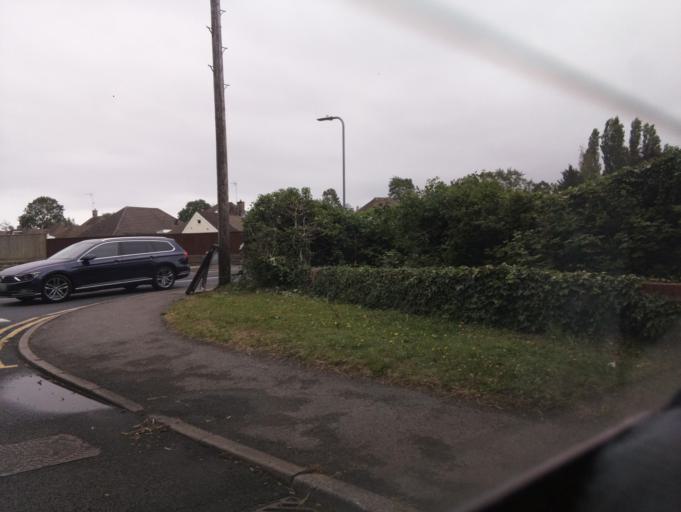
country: GB
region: Wales
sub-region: Vale of Glamorgan
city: Penarth
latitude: 51.4214
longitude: -3.1774
